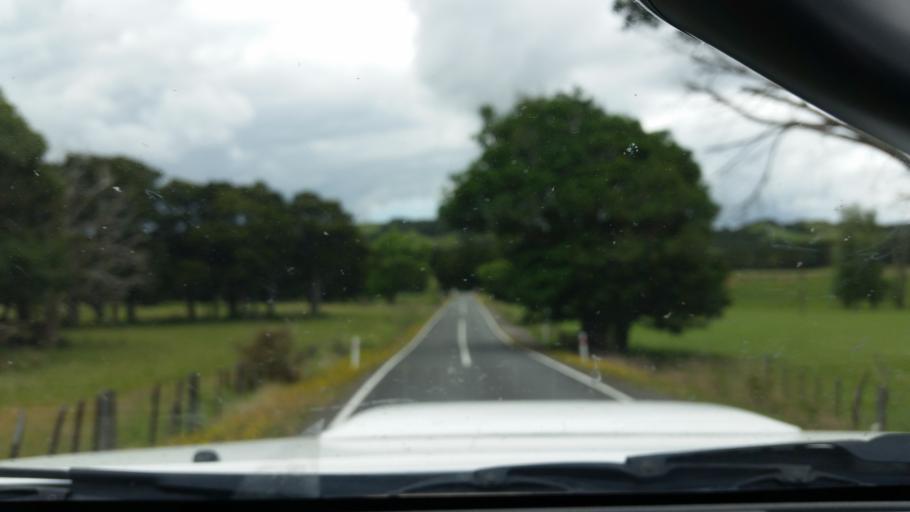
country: NZ
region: Northland
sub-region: Kaipara District
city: Dargaville
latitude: -35.8562
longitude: 173.8507
